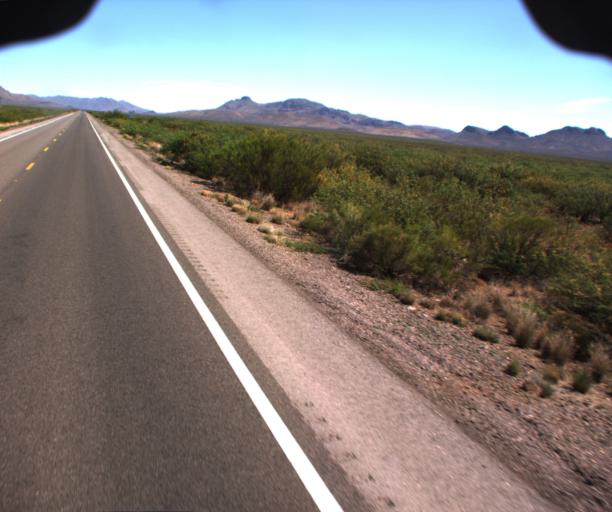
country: US
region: Arizona
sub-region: Cochise County
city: Douglas
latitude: 31.3925
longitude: -109.5103
